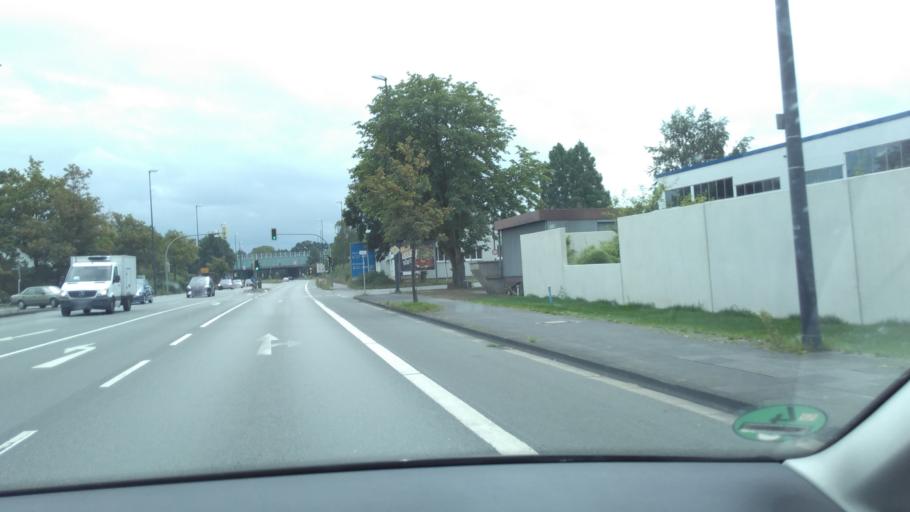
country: DE
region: North Rhine-Westphalia
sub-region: Regierungsbezirk Detmold
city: Guetersloh
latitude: 51.8842
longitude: 8.4271
